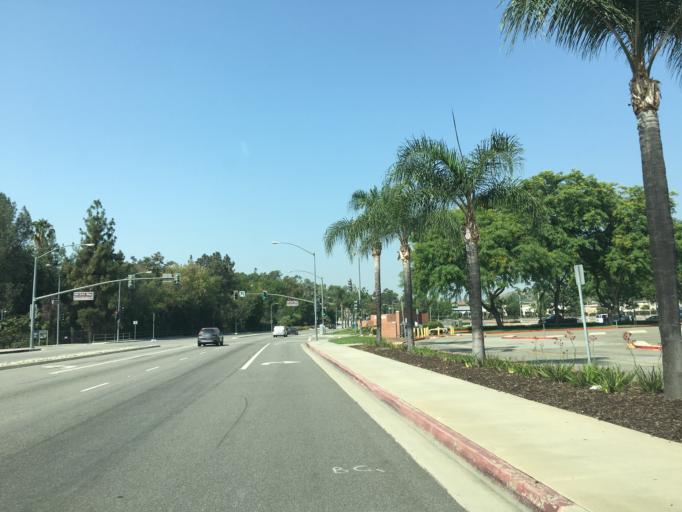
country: US
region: California
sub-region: Los Angeles County
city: Walnut
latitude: 34.0444
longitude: -117.8443
